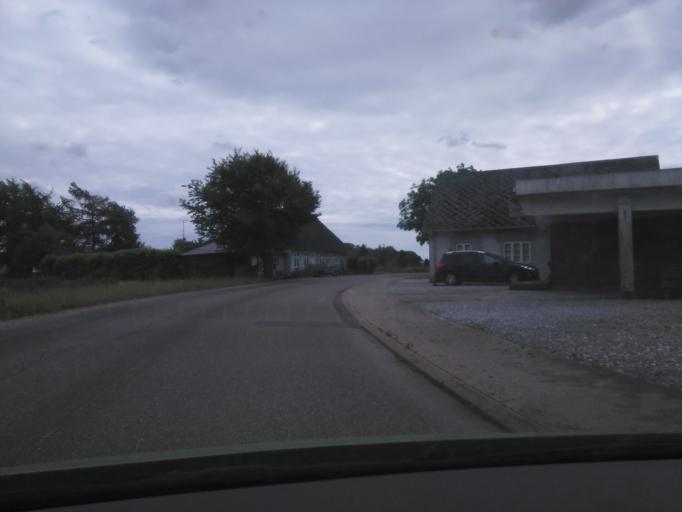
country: DK
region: Central Jutland
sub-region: Odder Kommune
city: Odder
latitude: 55.9980
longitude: 10.1144
